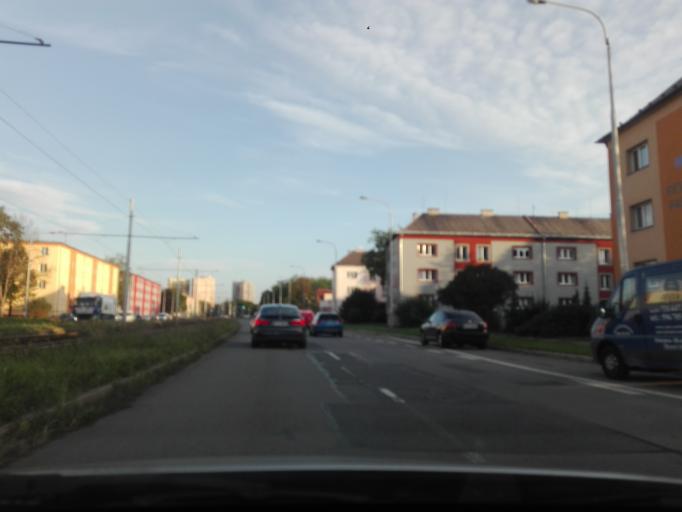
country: CZ
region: Moravskoslezsky
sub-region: Okres Ostrava-Mesto
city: Ostrava
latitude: 49.7892
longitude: 18.2550
